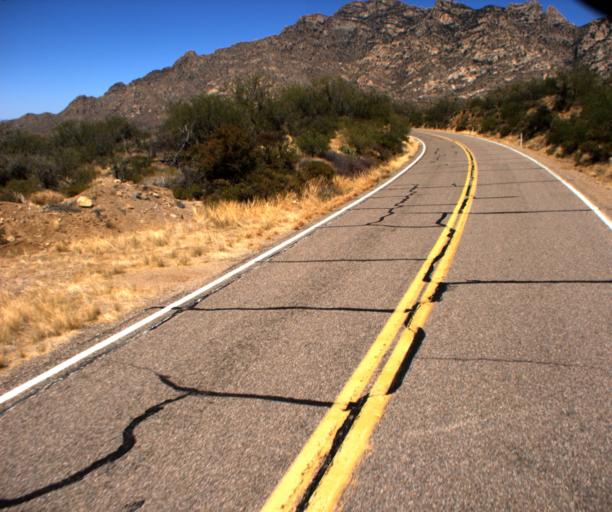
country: US
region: Arizona
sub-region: Pima County
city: Three Points
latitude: 31.9903
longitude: -111.5796
